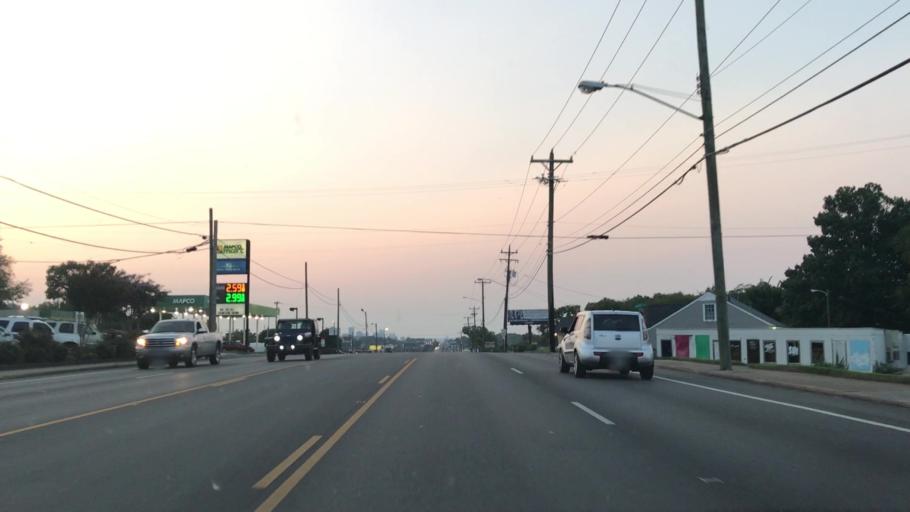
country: US
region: Tennessee
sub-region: Davidson County
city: Oak Hill
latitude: 36.1036
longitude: -86.7415
